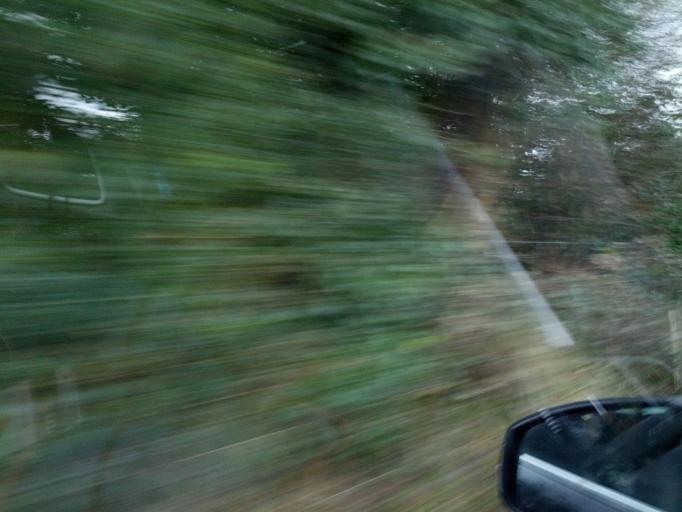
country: IE
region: Connaught
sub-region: County Galway
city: Athenry
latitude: 53.3874
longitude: -8.6567
